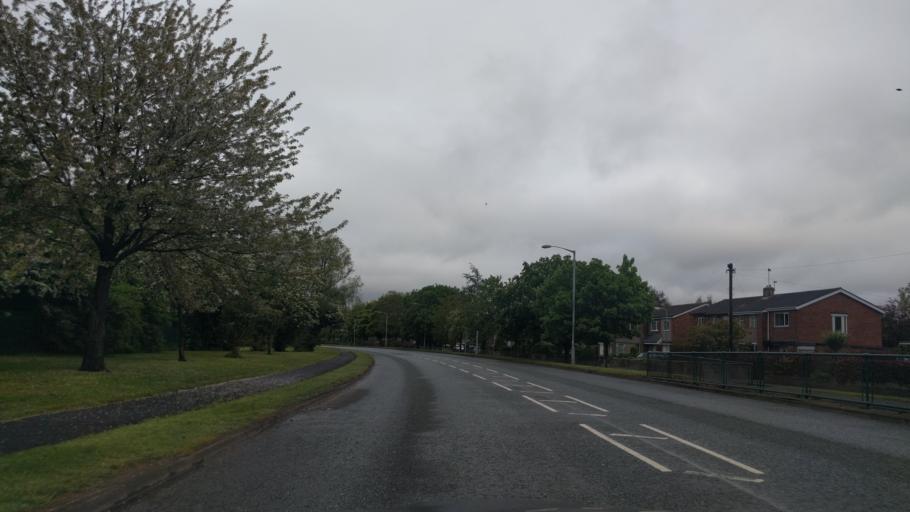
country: GB
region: England
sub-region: Northumberland
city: Morpeth
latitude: 55.1589
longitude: -1.6810
